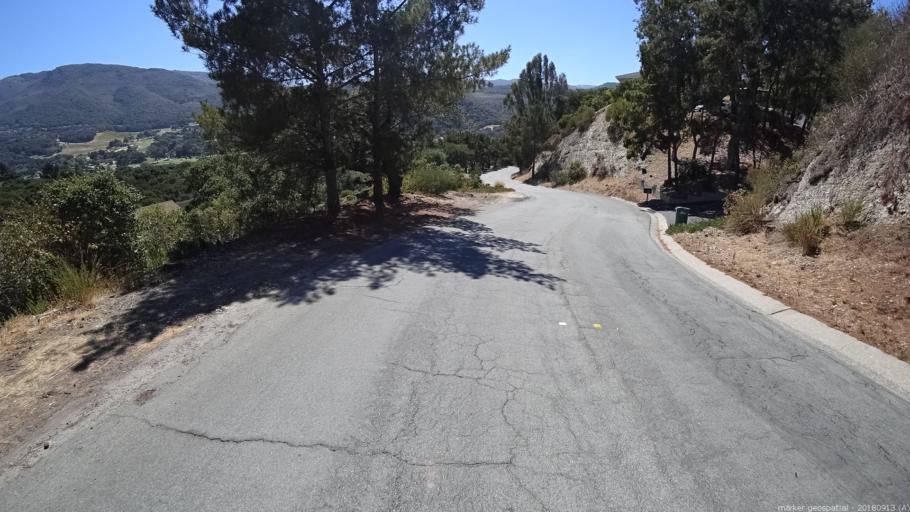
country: US
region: California
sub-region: Monterey County
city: Carmel Valley Village
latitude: 36.5246
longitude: -121.8060
